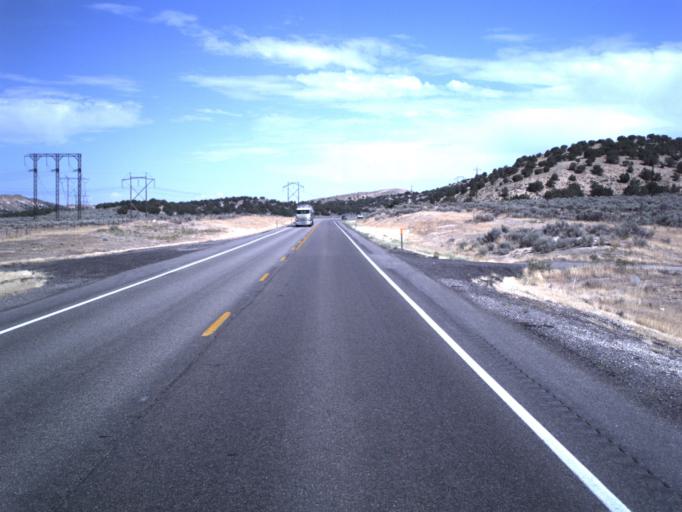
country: US
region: Utah
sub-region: Sanpete County
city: Gunnison
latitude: 39.3478
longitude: -111.9267
